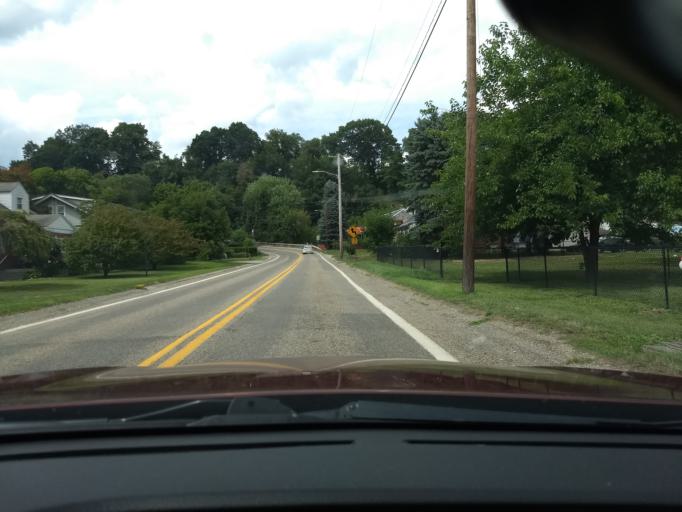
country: US
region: Pennsylvania
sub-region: Allegheny County
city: Cheswick
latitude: 40.5429
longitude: -79.8163
